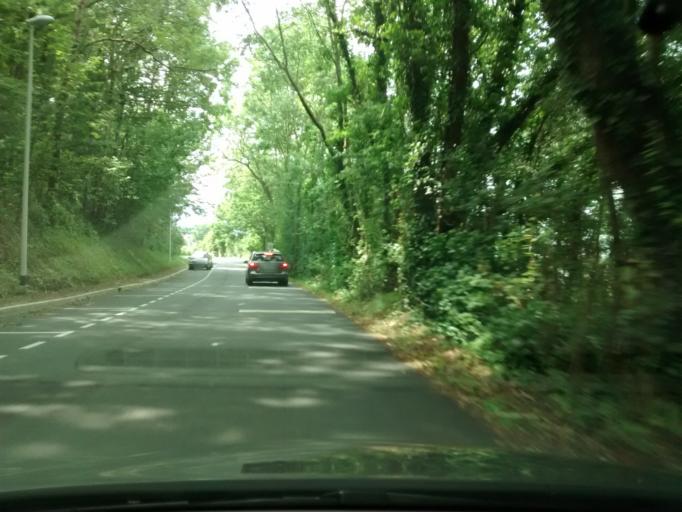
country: FR
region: Lower Normandy
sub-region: Departement du Calvados
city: Blonville-sur-Mer
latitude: 49.3427
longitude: 0.0437
